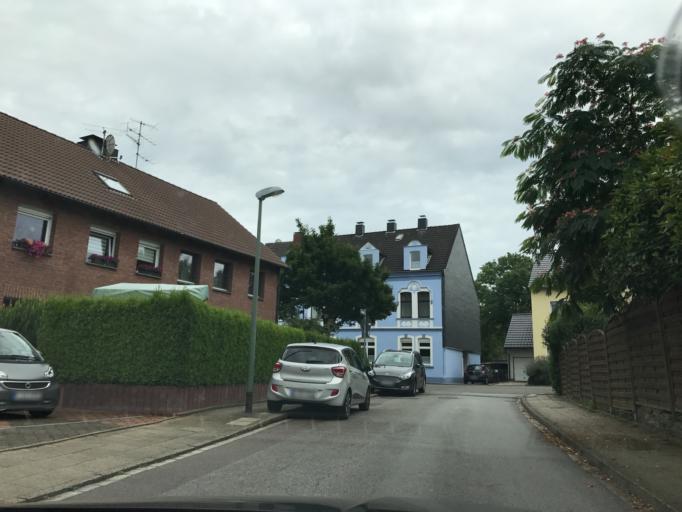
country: DE
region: North Rhine-Westphalia
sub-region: Regierungsbezirk Munster
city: Bottrop
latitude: 51.4811
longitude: 6.9536
